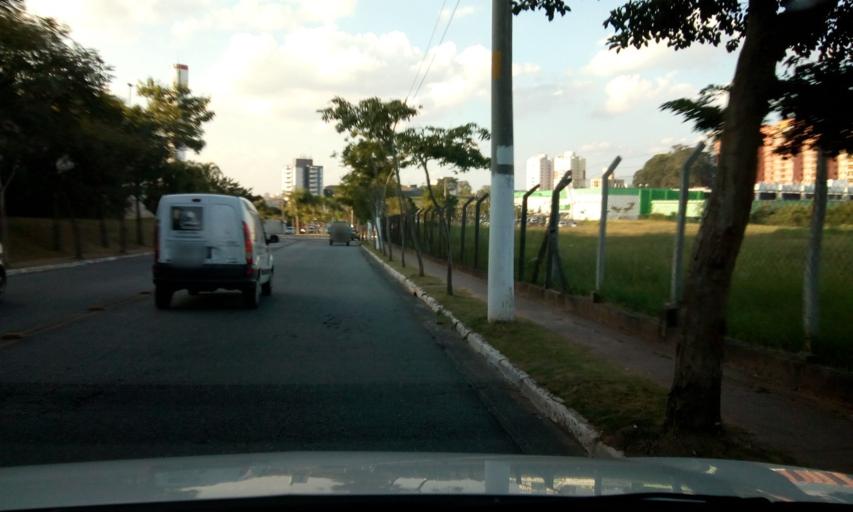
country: BR
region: Sao Paulo
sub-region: Diadema
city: Diadema
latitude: -23.6814
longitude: -46.6753
